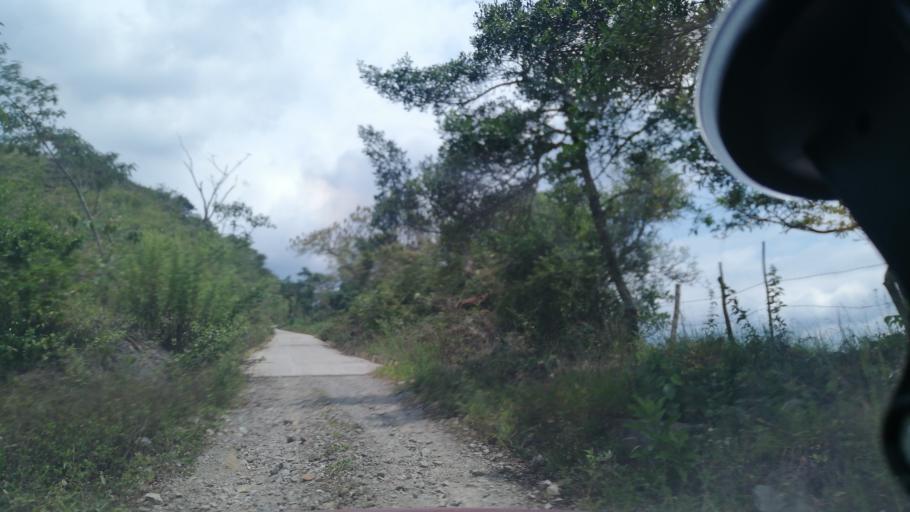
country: CO
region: Cundinamarca
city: Vergara
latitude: 5.2004
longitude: -74.2767
